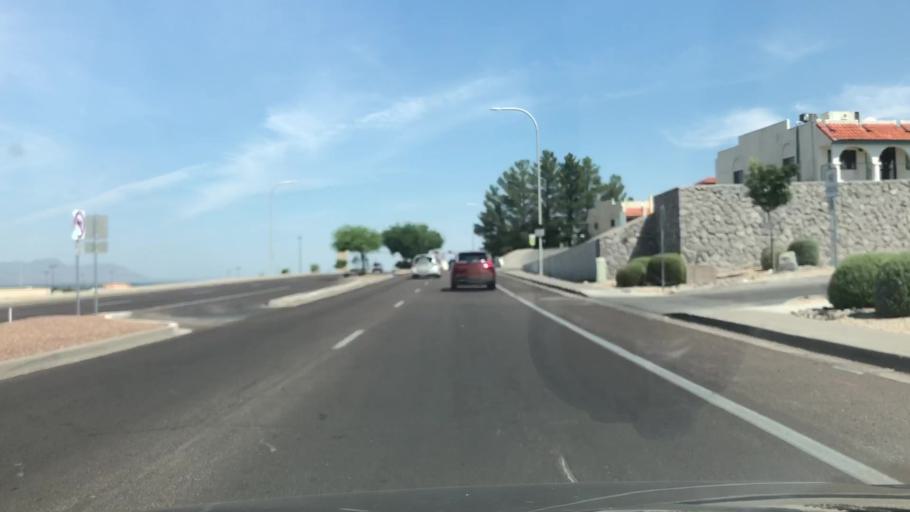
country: US
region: New Mexico
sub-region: Dona Ana County
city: University Park
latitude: 32.3107
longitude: -106.7408
